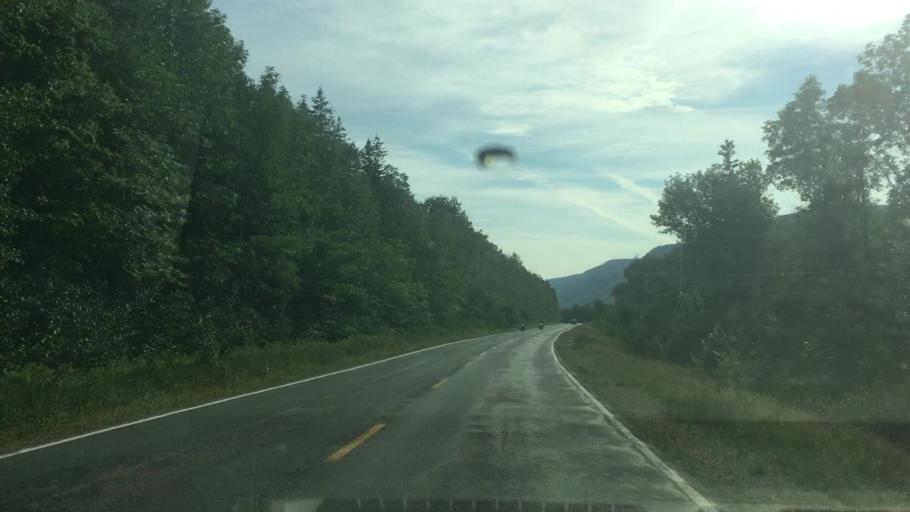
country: CA
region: Nova Scotia
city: Sydney Mines
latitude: 46.8617
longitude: -60.5660
